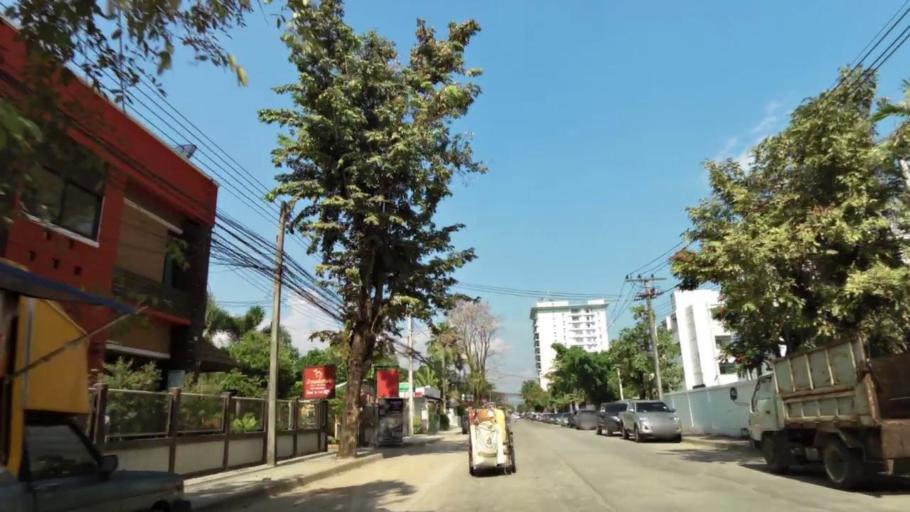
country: TH
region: Chiang Rai
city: Chiang Rai
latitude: 19.8980
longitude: 99.8278
